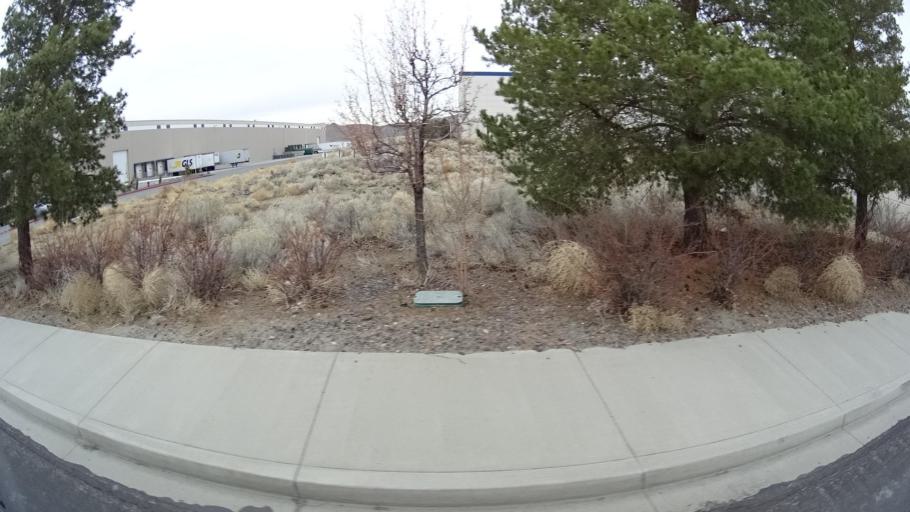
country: US
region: Nevada
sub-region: Washoe County
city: Spanish Springs
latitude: 39.6732
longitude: -119.7066
